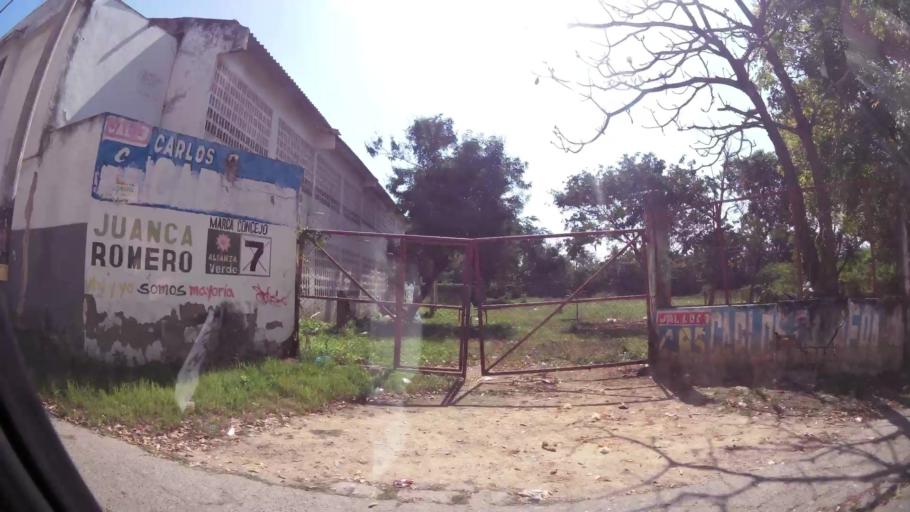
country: CO
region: Bolivar
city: Cartagena
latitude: 10.3855
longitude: -75.4715
